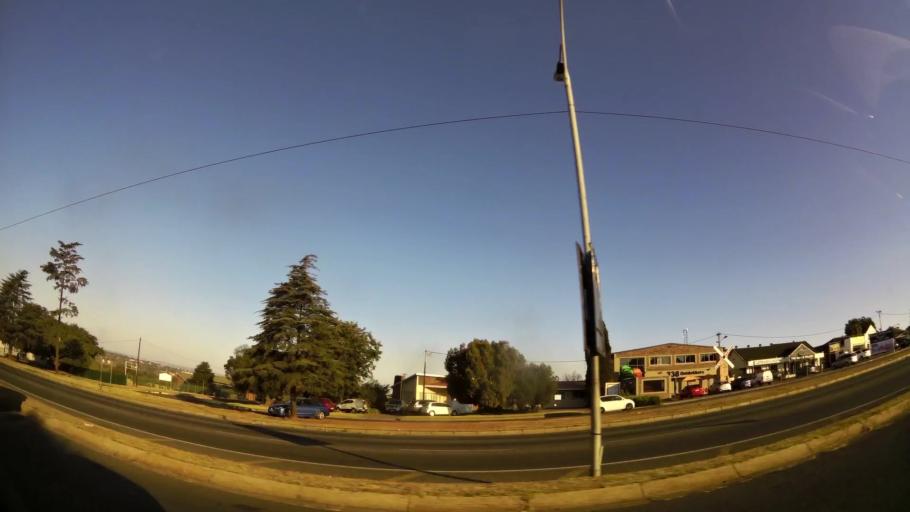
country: ZA
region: Gauteng
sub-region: City of Johannesburg Metropolitan Municipality
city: Roodepoort
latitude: -26.1472
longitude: 27.8942
